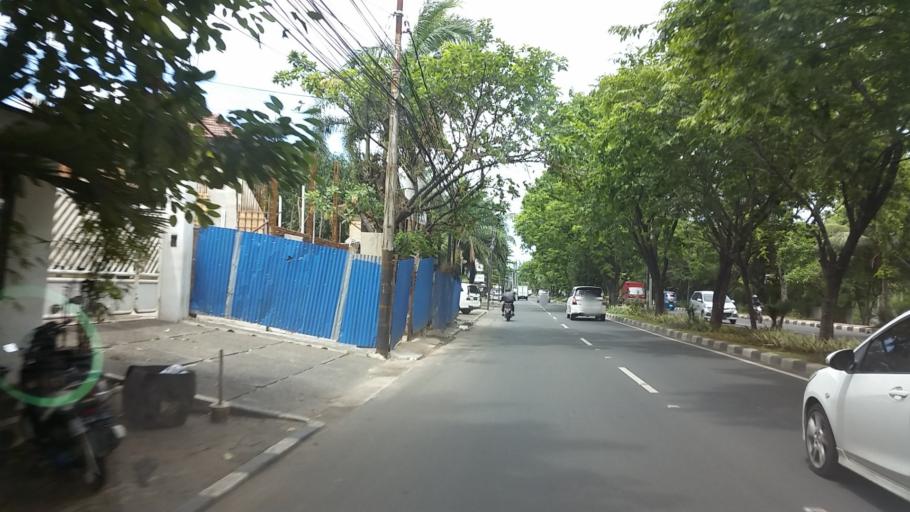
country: ID
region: Jakarta Raya
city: Jakarta
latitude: -6.1214
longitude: 106.7941
